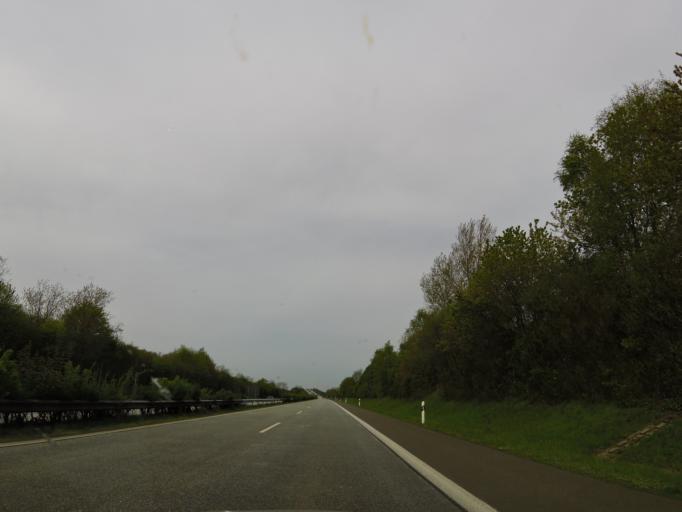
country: DE
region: Schleswig-Holstein
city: Besdorf
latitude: 54.0624
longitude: 9.3506
